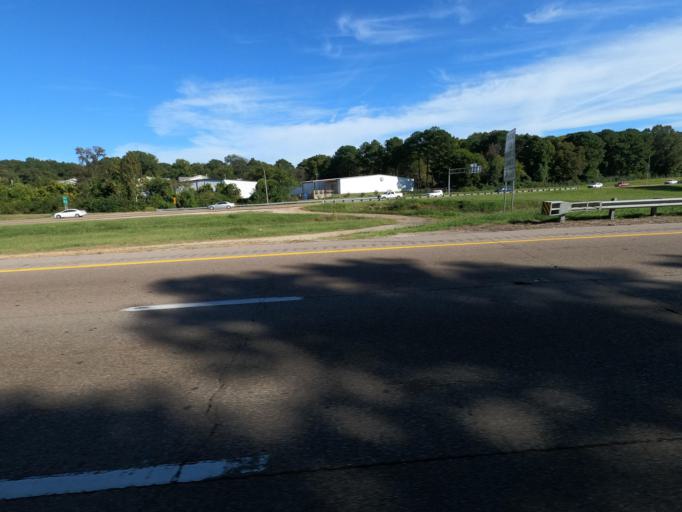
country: US
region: Tennessee
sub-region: Shelby County
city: New South Memphis
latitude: 35.0773
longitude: -90.0263
